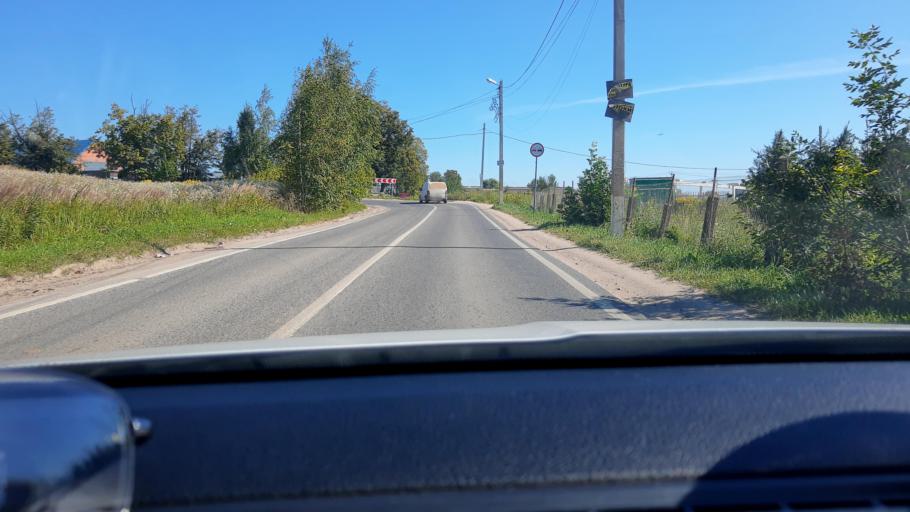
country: RU
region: Moskovskaya
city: Petrovo-Dal'neye
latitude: 55.7700
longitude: 37.2223
